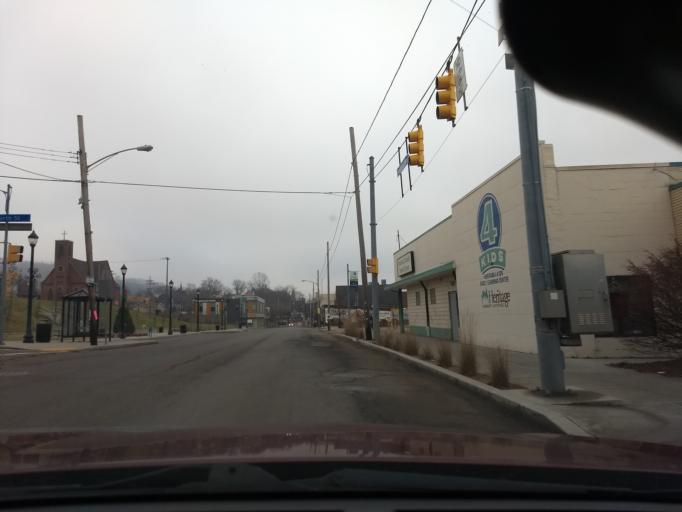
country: US
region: Pennsylvania
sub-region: Allegheny County
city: Braddock
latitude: 40.4050
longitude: -79.8714
